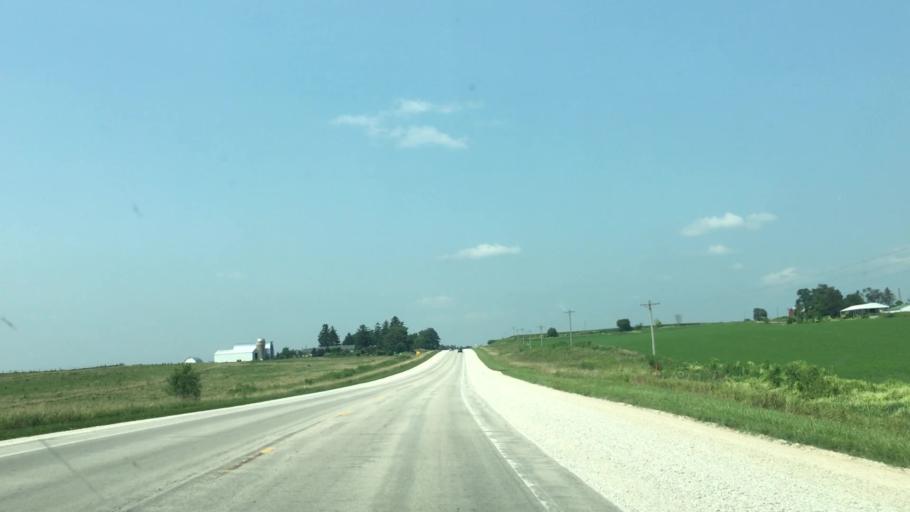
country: US
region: Iowa
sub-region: Winneshiek County
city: Decorah
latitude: 43.4158
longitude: -91.8592
